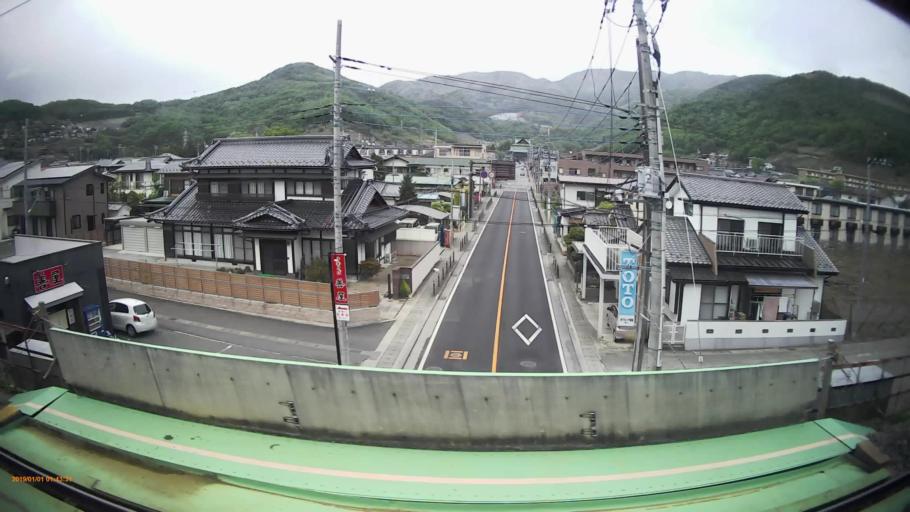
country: JP
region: Yamanashi
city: Kofu-shi
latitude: 35.6606
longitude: 138.5915
